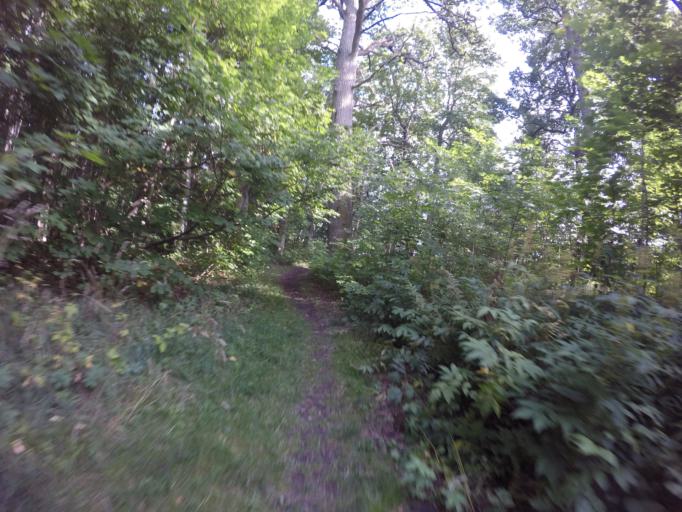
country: SE
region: Soedermanland
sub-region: Eskilstuna Kommun
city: Kvicksund
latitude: 59.4798
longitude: 16.2903
